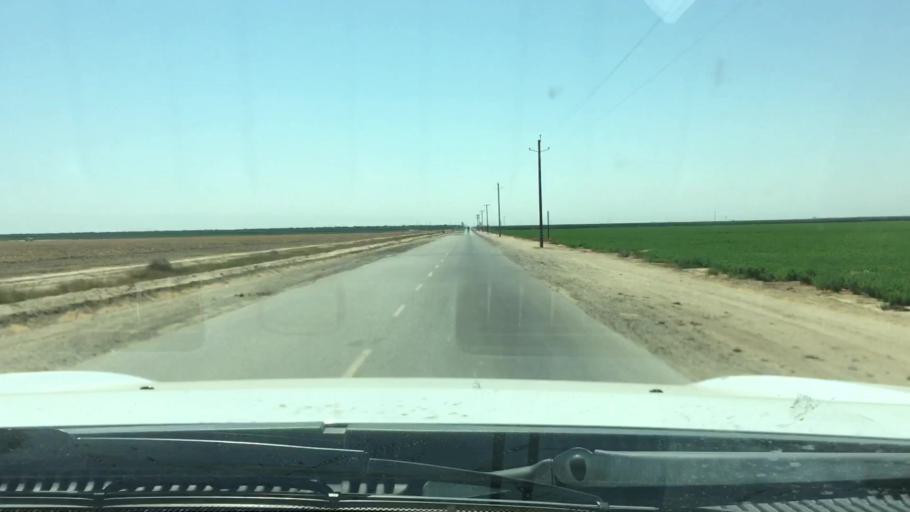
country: US
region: California
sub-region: Kern County
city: Wasco
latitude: 35.5870
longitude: -119.4026
